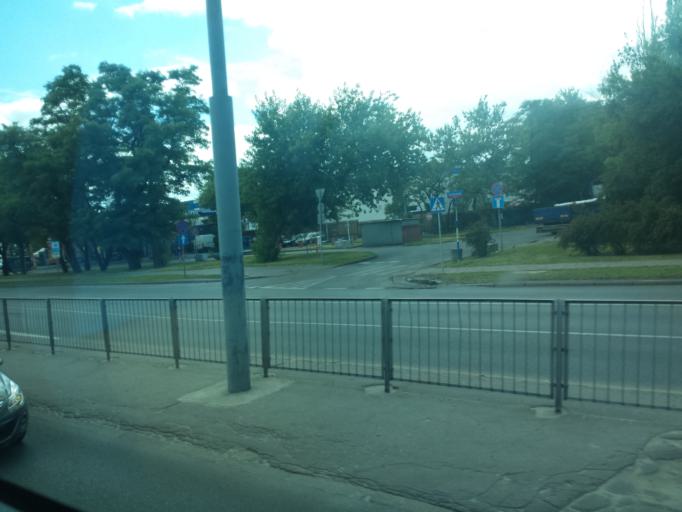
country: PL
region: Masovian Voivodeship
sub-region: Warszawa
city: Praga Poludnie
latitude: 52.2382
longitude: 21.1183
